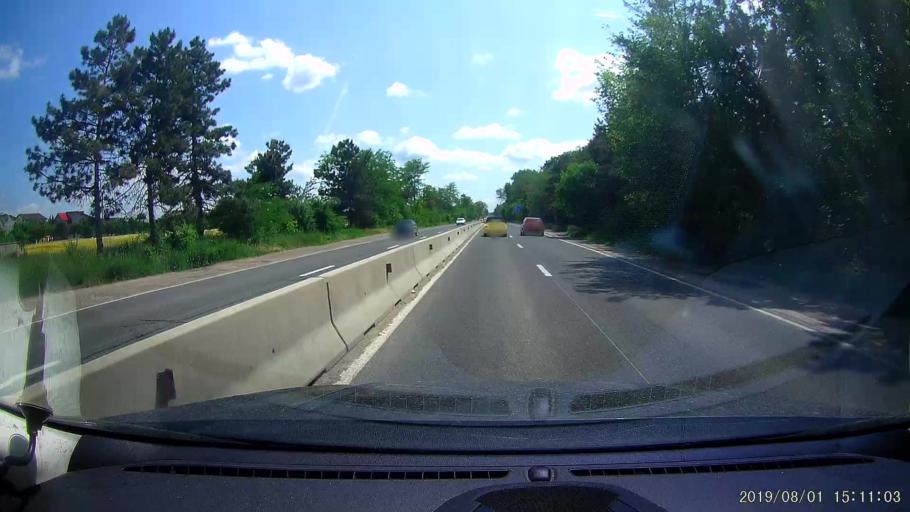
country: RO
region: Braila
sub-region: Comuna Chiscani
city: Chiscani
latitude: 45.2214
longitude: 27.9275
